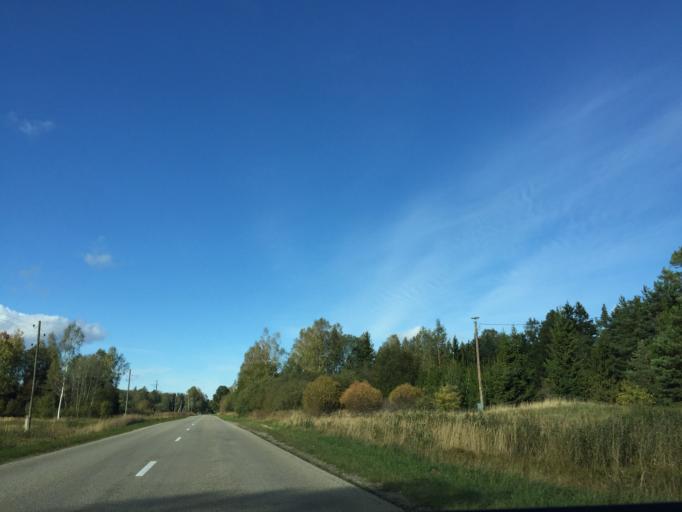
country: LV
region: Rojas
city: Roja
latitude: 57.4290
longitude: 22.9139
